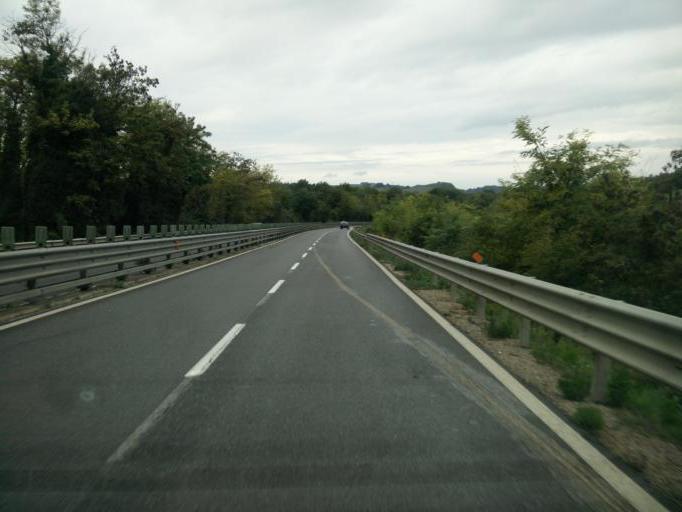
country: IT
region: Tuscany
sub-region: Provincia di Siena
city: Colle di Val d'Elsa
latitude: 43.4237
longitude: 11.1473
